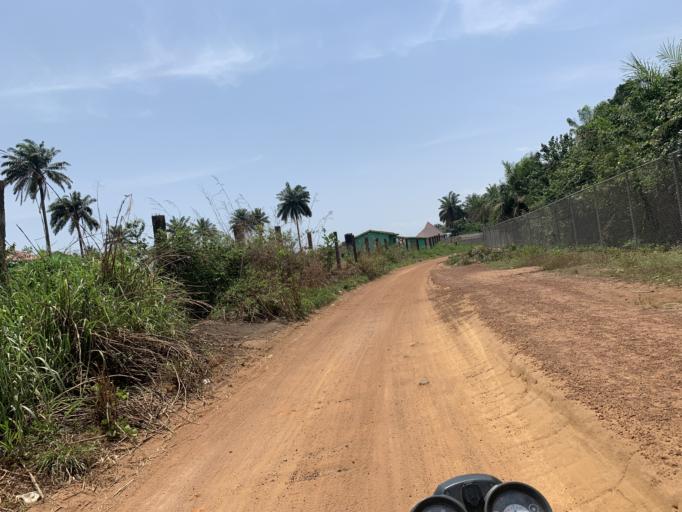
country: SL
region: Western Area
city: Waterloo
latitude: 8.3373
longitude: -13.0349
